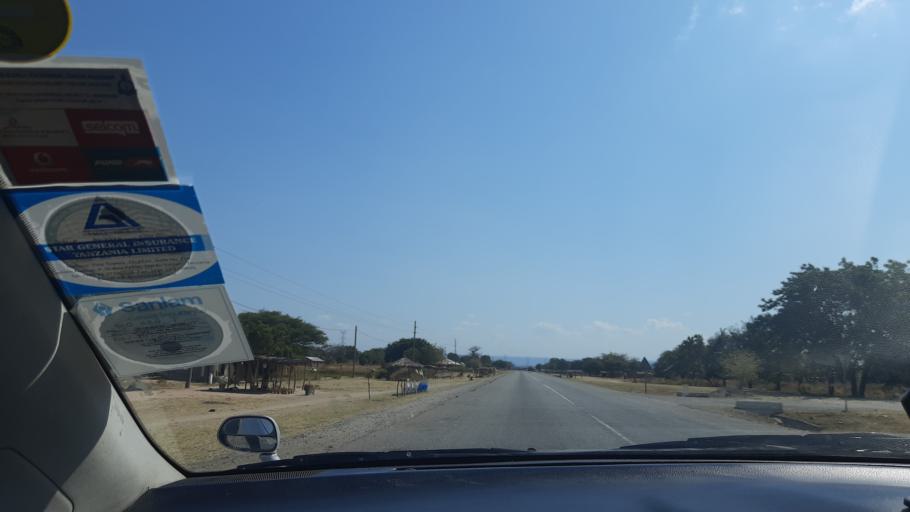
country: TZ
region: Singida
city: Kintinku
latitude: -5.8786
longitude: 35.1258
